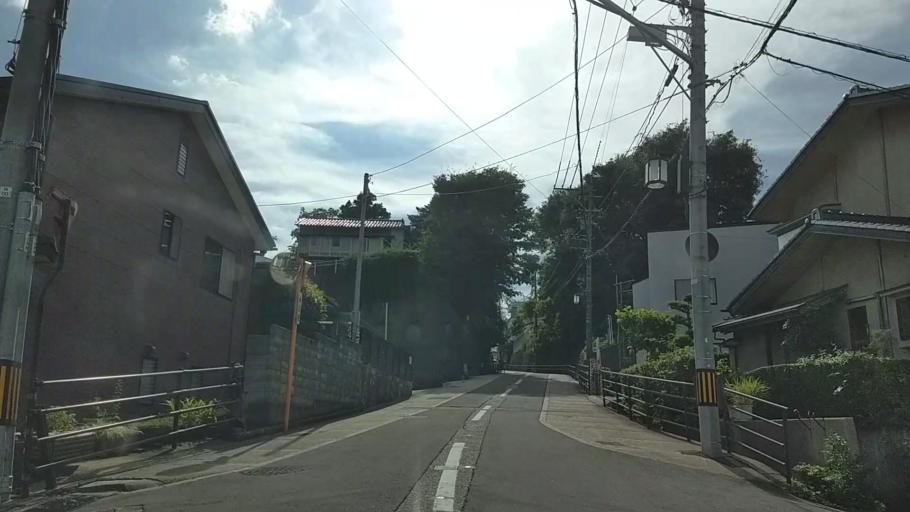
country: JP
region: Ishikawa
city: Nonoichi
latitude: 36.5468
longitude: 136.6612
